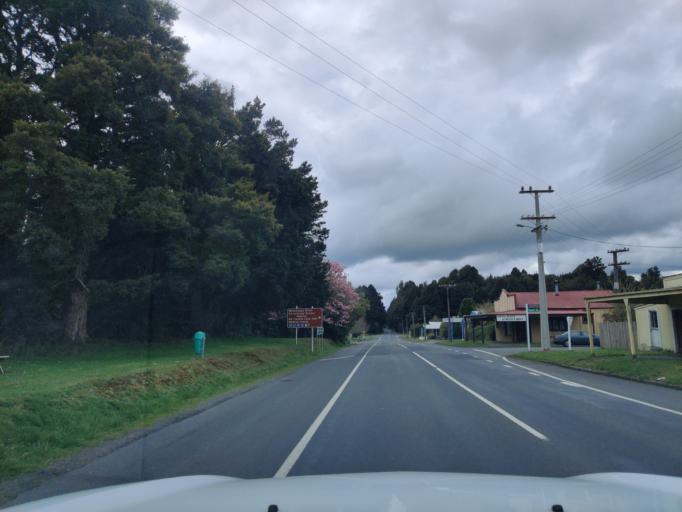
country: NZ
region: Waikato
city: Turangi
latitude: -38.9989
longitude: 175.3775
